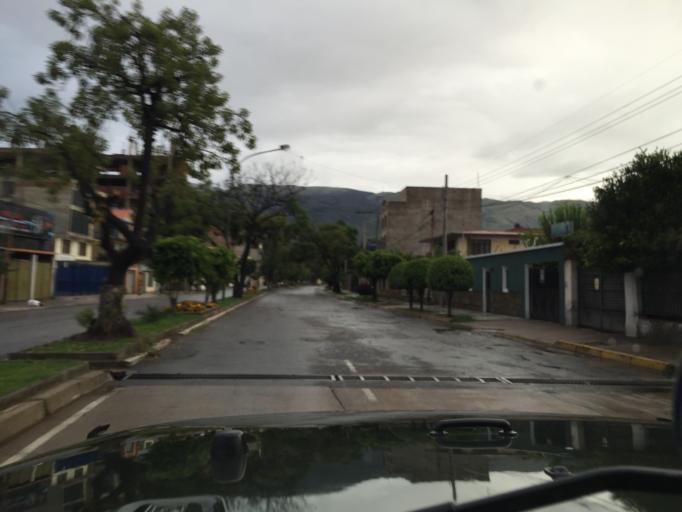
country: BO
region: Cochabamba
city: Cochabamba
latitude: -17.3864
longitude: -66.1656
